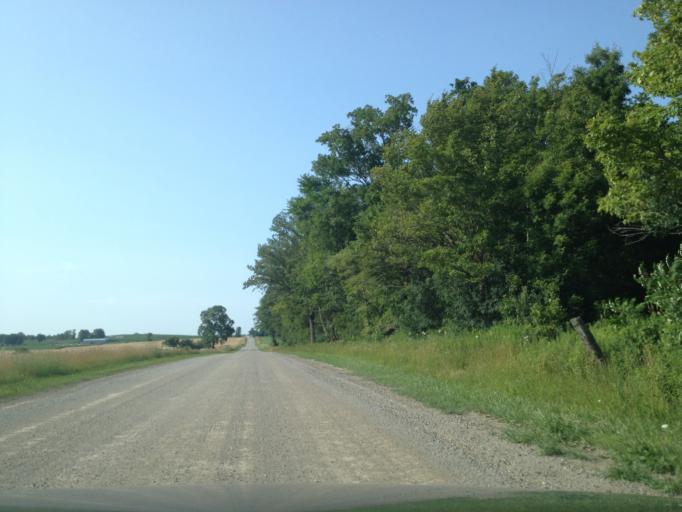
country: CA
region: Ontario
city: Ingersoll
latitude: 42.9519
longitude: -80.7725
